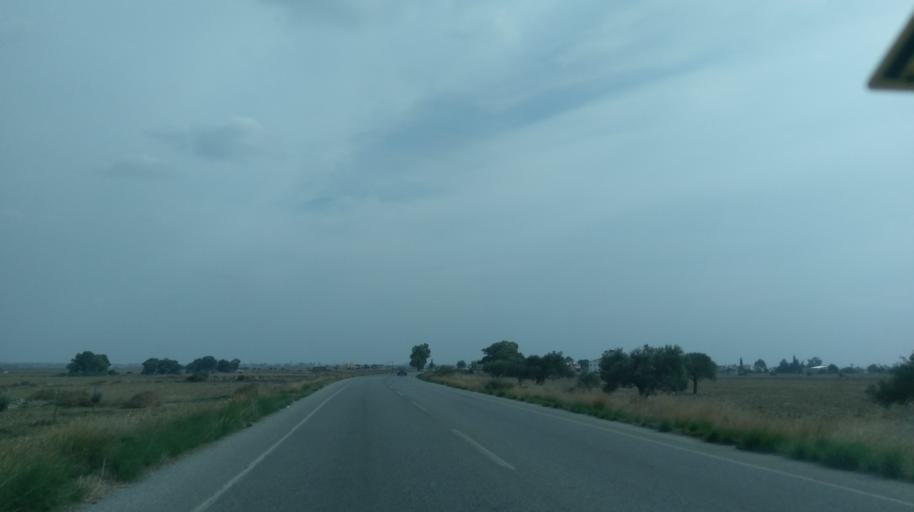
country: CY
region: Ammochostos
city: Lefkonoiko
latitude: 35.2580
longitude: 33.6776
